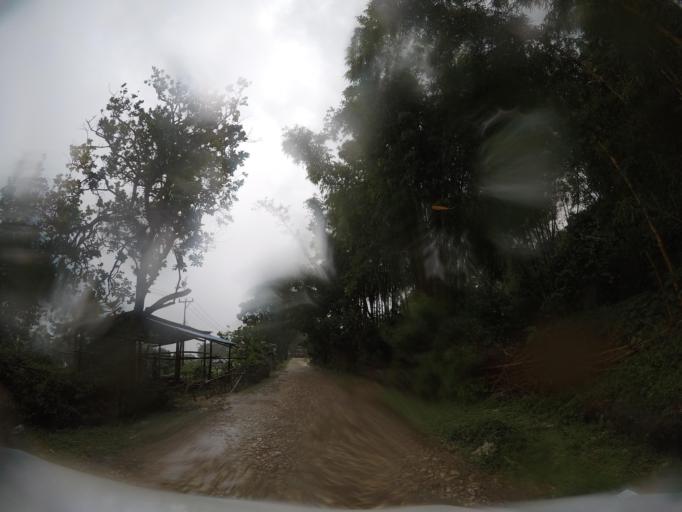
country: TL
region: Baucau
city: Venilale
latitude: -8.6426
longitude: 126.3976
